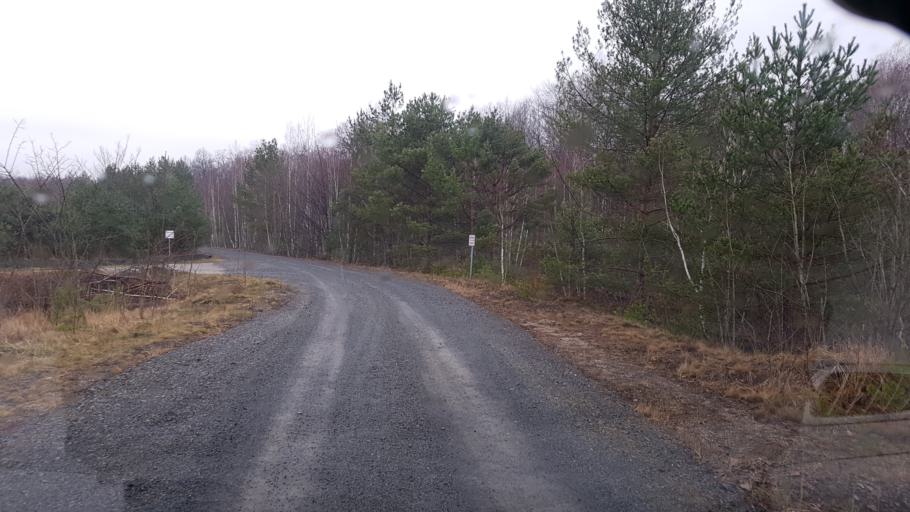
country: DE
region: Brandenburg
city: Lauchhammer
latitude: 51.4933
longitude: 13.8114
